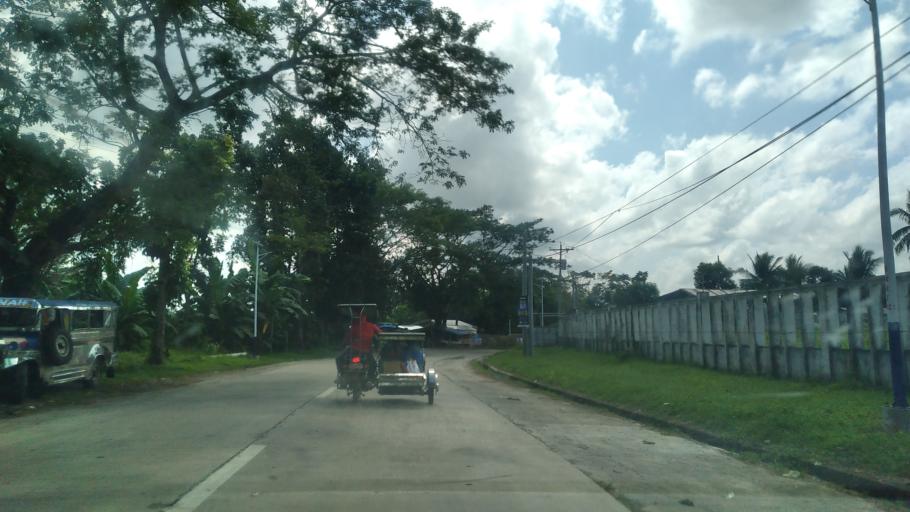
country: PH
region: Calabarzon
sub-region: Province of Quezon
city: Macalelon
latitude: 13.7576
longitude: 122.1429
